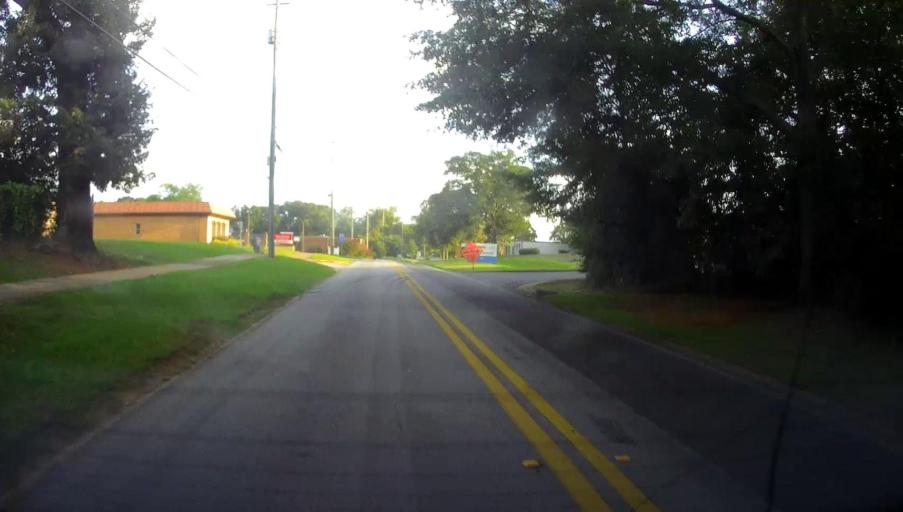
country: US
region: Georgia
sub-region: Monroe County
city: Forsyth
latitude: 33.0325
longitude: -83.9464
